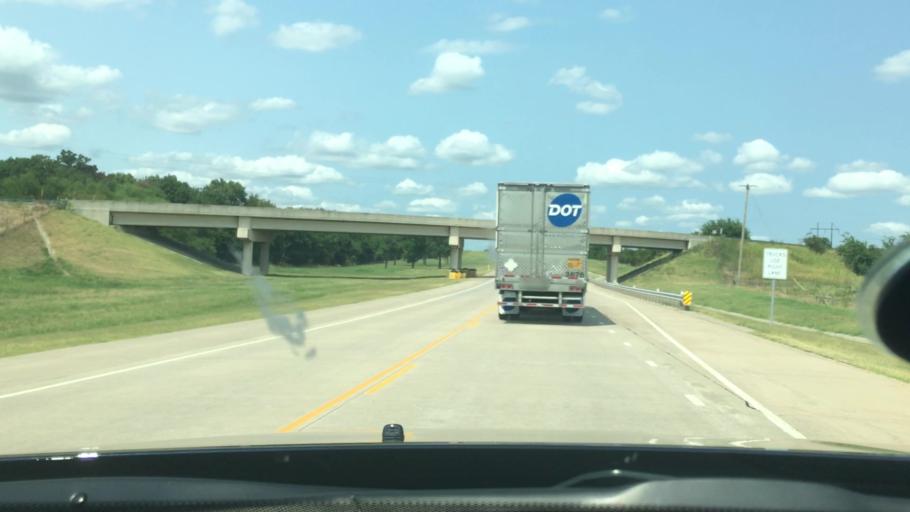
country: US
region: Oklahoma
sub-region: Murray County
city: Sulphur
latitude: 34.5923
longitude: -96.8967
